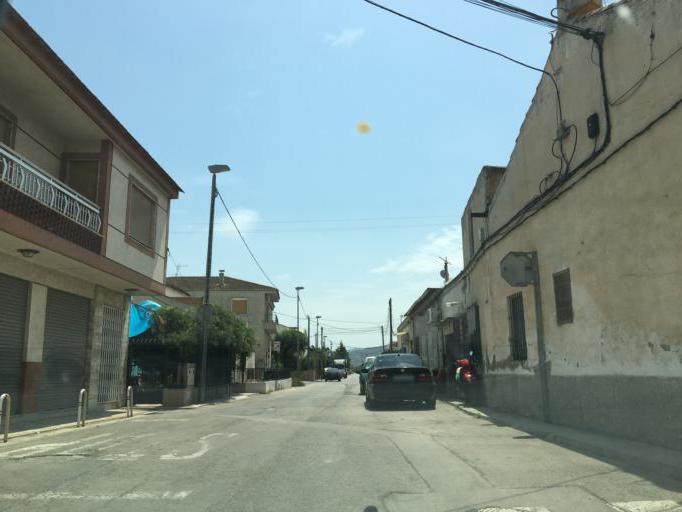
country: ES
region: Murcia
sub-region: Murcia
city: Santomera
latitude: 38.0280
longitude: -1.0492
